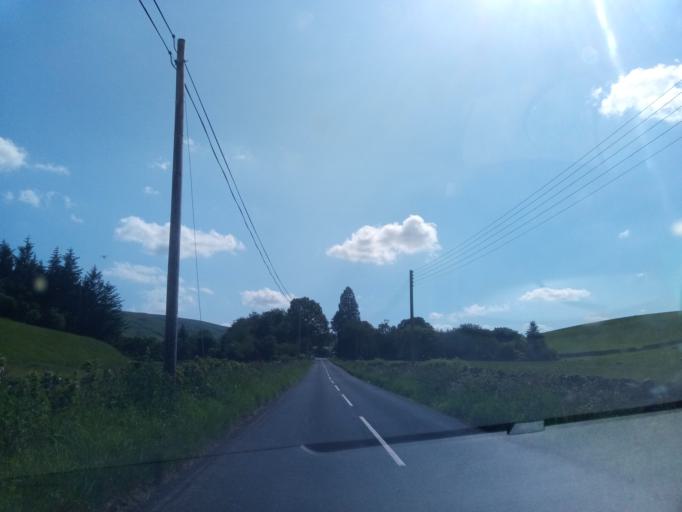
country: GB
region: Scotland
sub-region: The Scottish Borders
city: Innerleithen
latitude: 55.5271
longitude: -3.0409
